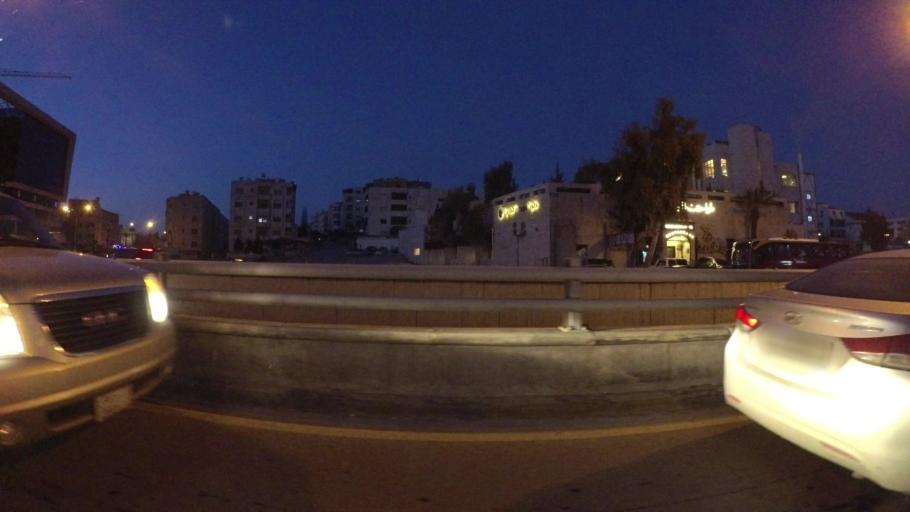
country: JO
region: Amman
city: Al Jubayhah
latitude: 31.9920
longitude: 35.8664
